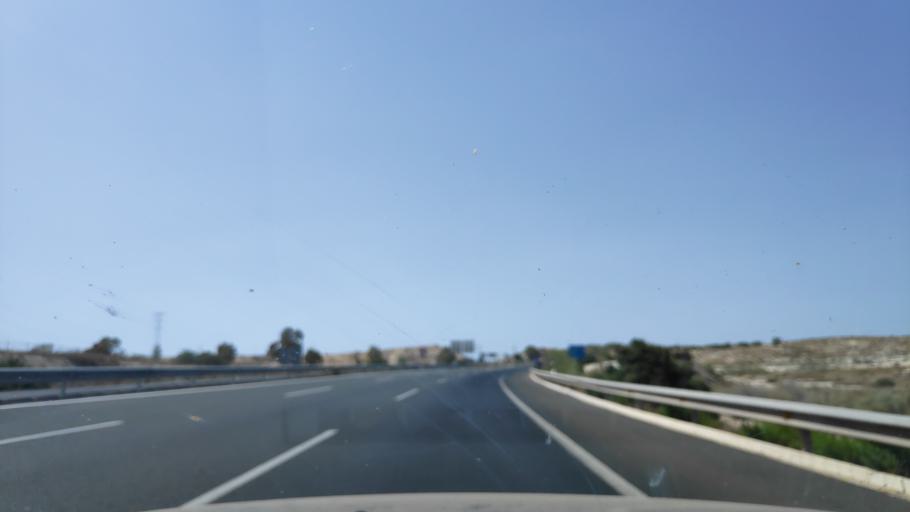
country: ES
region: Murcia
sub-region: Murcia
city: Murcia
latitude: 37.8759
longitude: -1.1290
